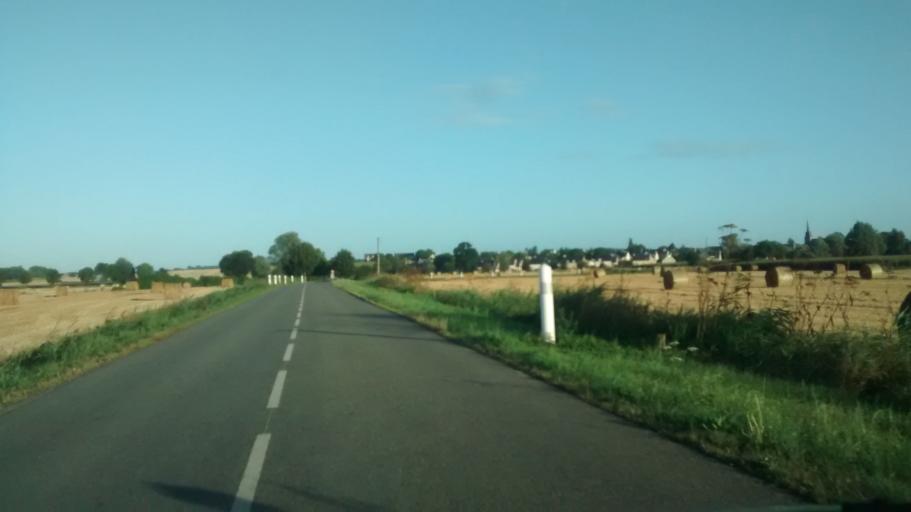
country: FR
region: Brittany
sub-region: Departement d'Ille-et-Vilaine
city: La Gouesniere
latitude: 48.5699
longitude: -1.8785
